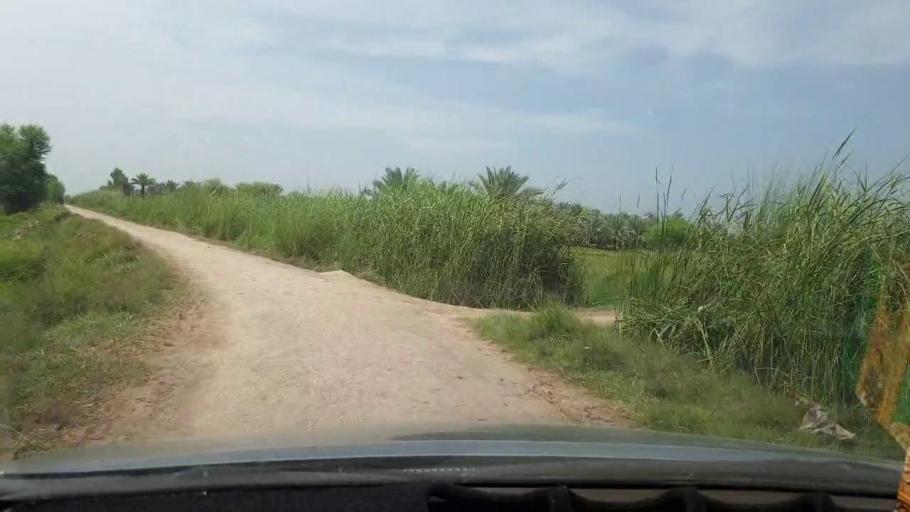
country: PK
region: Sindh
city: Khairpur
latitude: 27.4813
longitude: 68.7456
